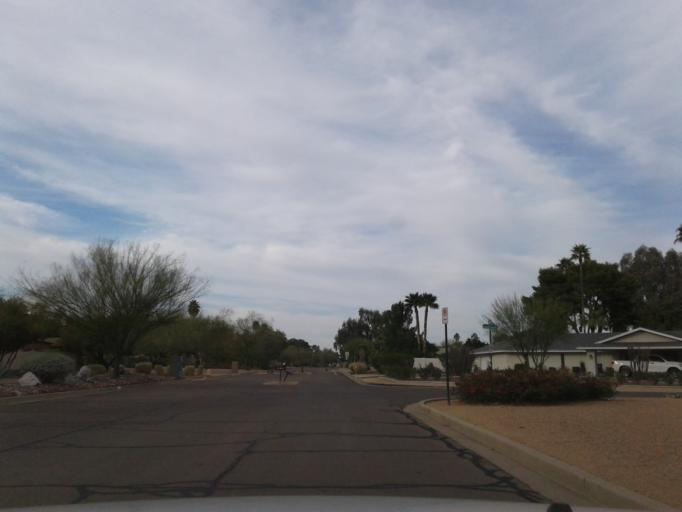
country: US
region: Arizona
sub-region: Maricopa County
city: Paradise Valley
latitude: 33.5777
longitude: -111.9359
